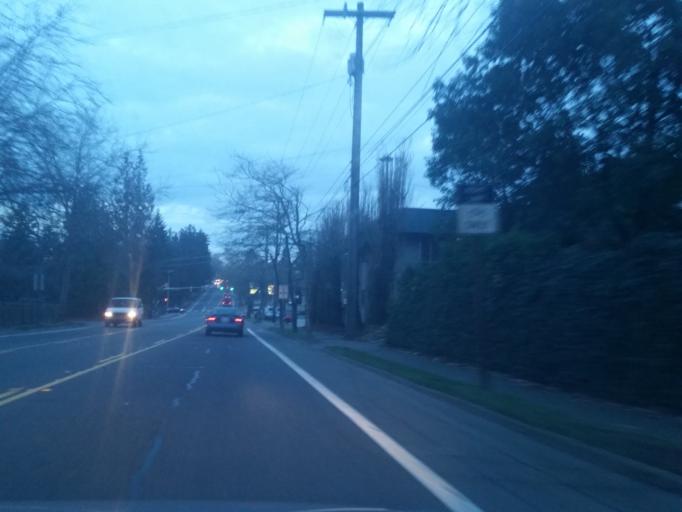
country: US
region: Washington
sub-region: King County
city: Shoreline
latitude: 47.7505
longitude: -122.3133
